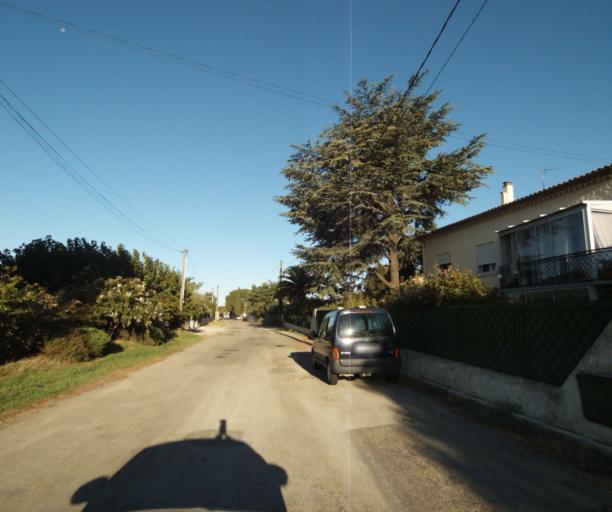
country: FR
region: Languedoc-Roussillon
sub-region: Departement du Gard
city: Bouillargues
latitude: 43.7965
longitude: 4.4237
